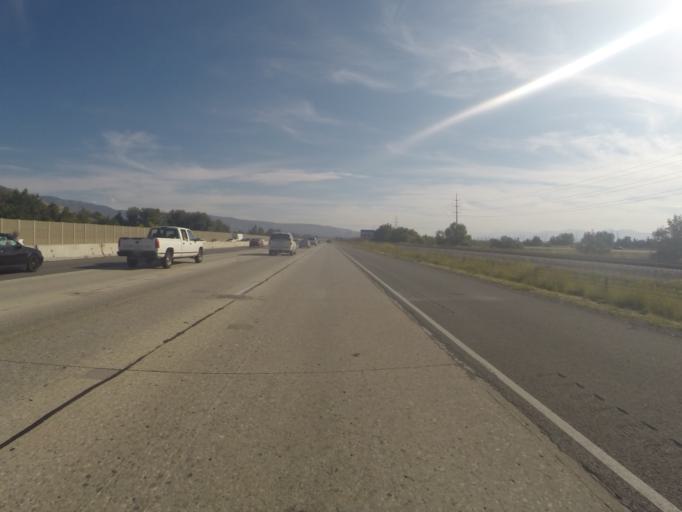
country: US
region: Utah
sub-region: Davis County
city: Centerville
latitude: 40.9454
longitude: -111.8912
